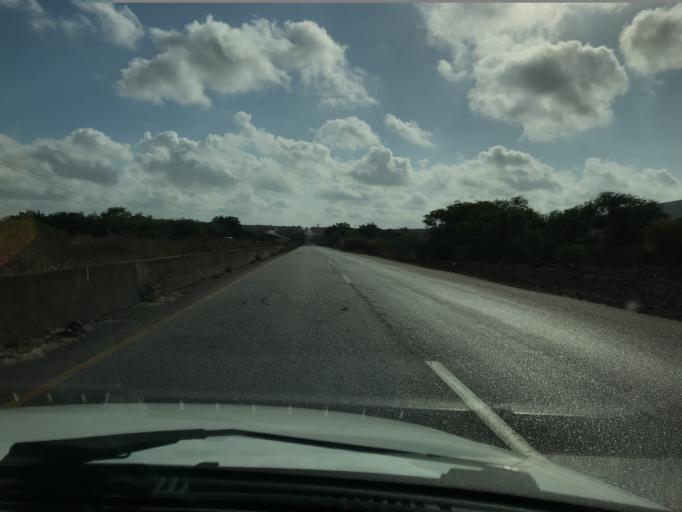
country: BR
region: Pernambuco
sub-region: Bezerros
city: Bezerros
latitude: -8.2305
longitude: -35.7067
